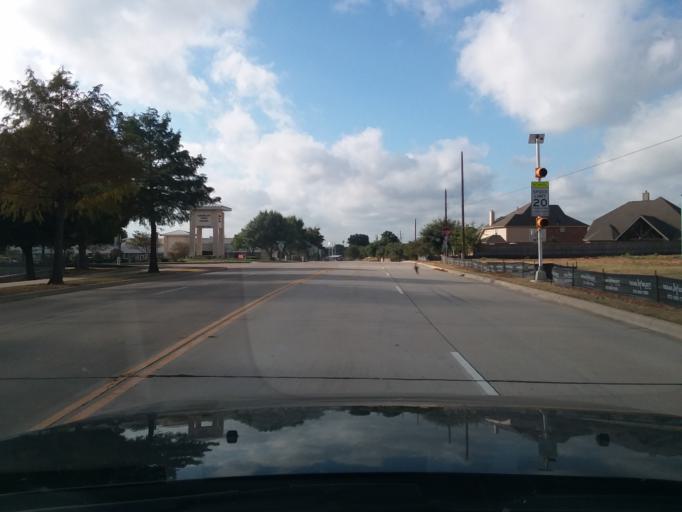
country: US
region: Texas
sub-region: Denton County
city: Hickory Creek
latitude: 33.1269
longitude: -97.0473
